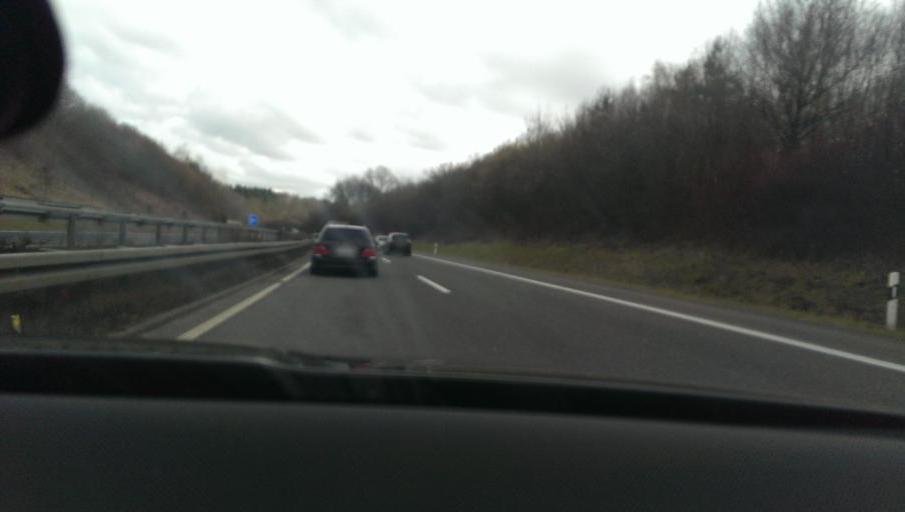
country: DE
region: Hesse
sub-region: Regierungsbezirk Darmstadt
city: Steinau an der Strasse
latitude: 50.3085
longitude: 9.4222
